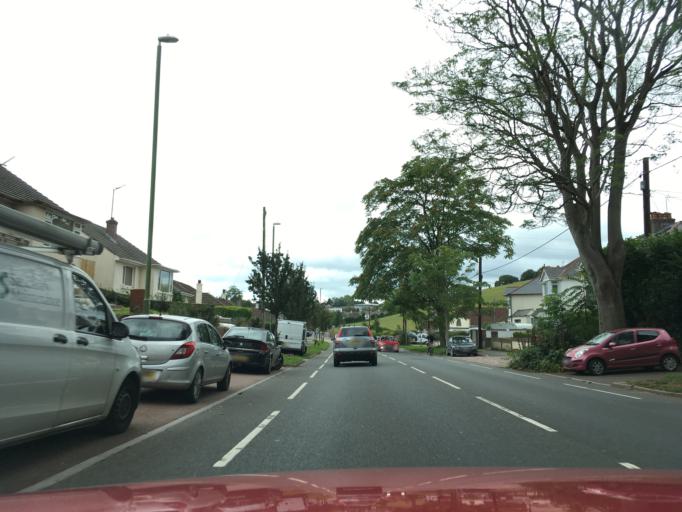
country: GB
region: England
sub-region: Borough of Torbay
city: Paignton
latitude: 50.4333
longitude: -3.5887
